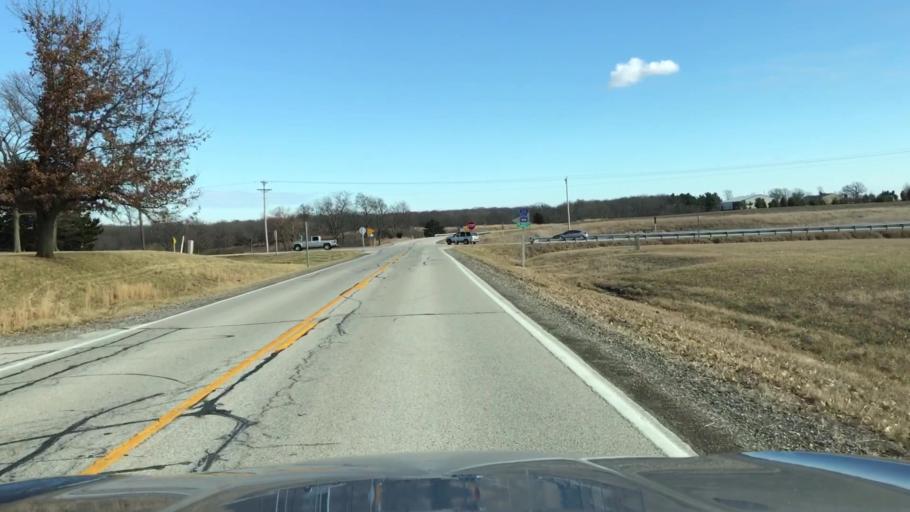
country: US
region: Illinois
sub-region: McLean County
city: Gridley
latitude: 40.6564
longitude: -88.9006
